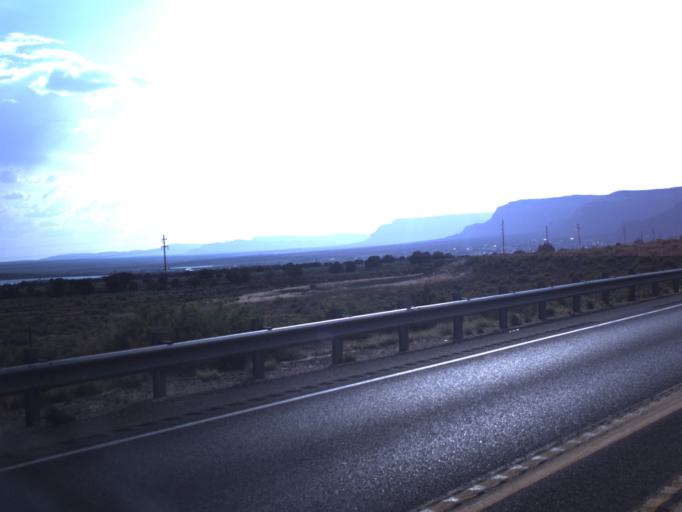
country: US
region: Utah
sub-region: Kane County
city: Kanab
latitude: 37.0296
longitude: -112.4878
